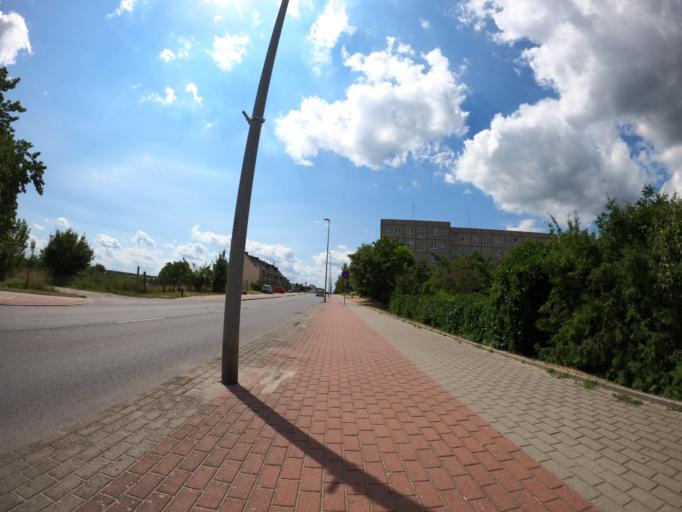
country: PL
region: West Pomeranian Voivodeship
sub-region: Powiat gryfinski
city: Gryfino
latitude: 53.2566
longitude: 14.5031
